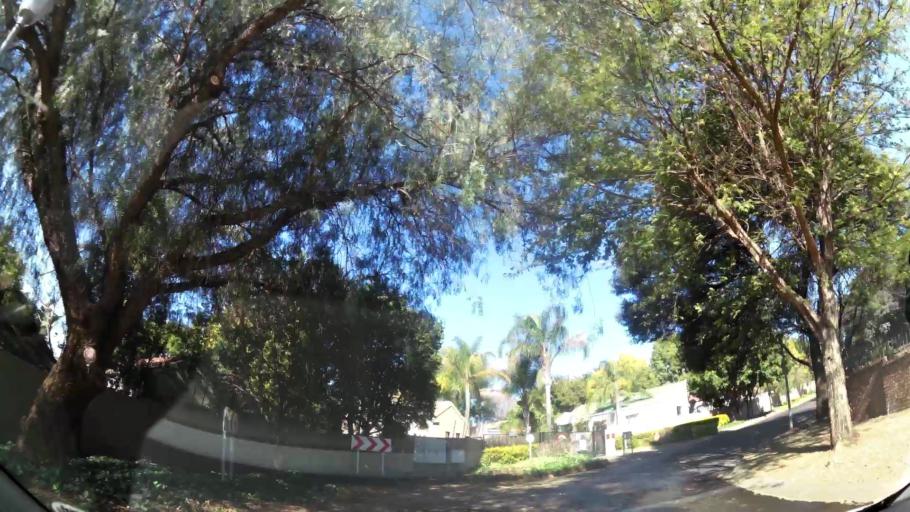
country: ZA
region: Gauteng
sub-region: City of Tshwane Metropolitan Municipality
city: Centurion
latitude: -25.8544
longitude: 28.1775
